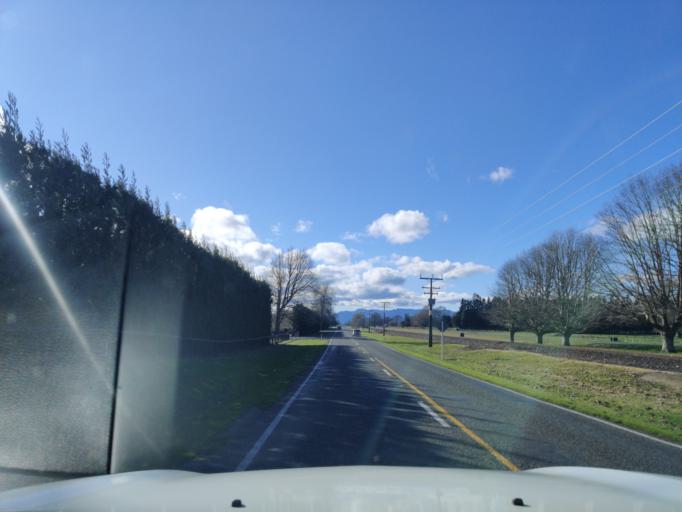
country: NZ
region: Waikato
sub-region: Matamata-Piako District
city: Matamata
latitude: -37.8516
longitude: 175.7588
